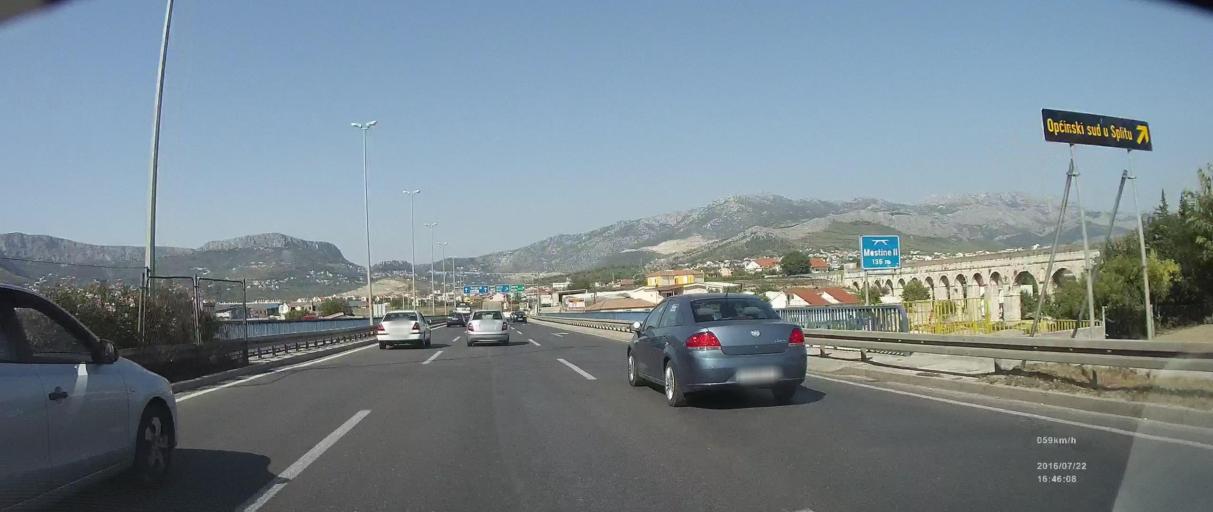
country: HR
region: Splitsko-Dalmatinska
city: Solin
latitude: 43.5240
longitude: 16.4877
